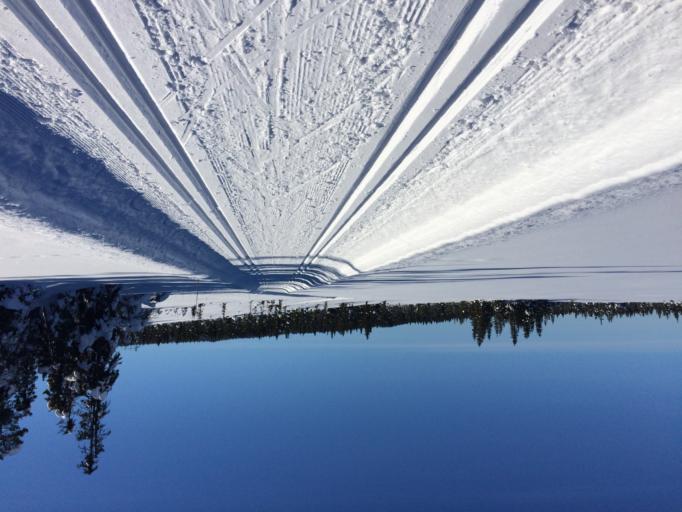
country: NO
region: Oppland
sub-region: Gausdal
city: Segalstad bru
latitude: 61.3264
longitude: 10.0839
